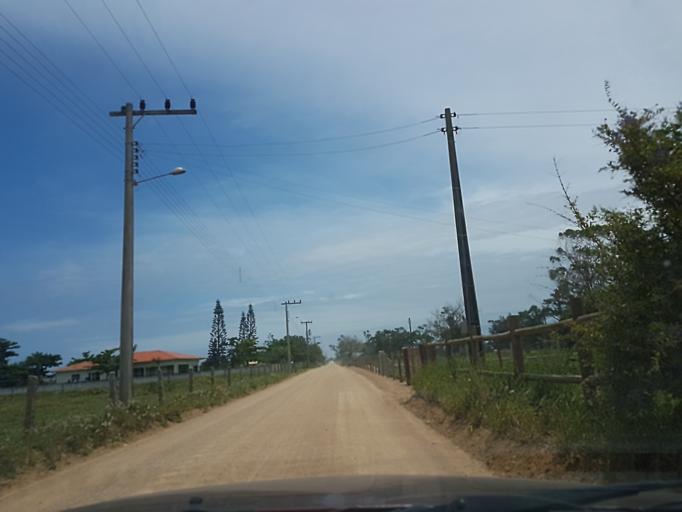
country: BR
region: Santa Catarina
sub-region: Jaguaruna
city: Jaguaruna
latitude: -28.6347
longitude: -48.9571
